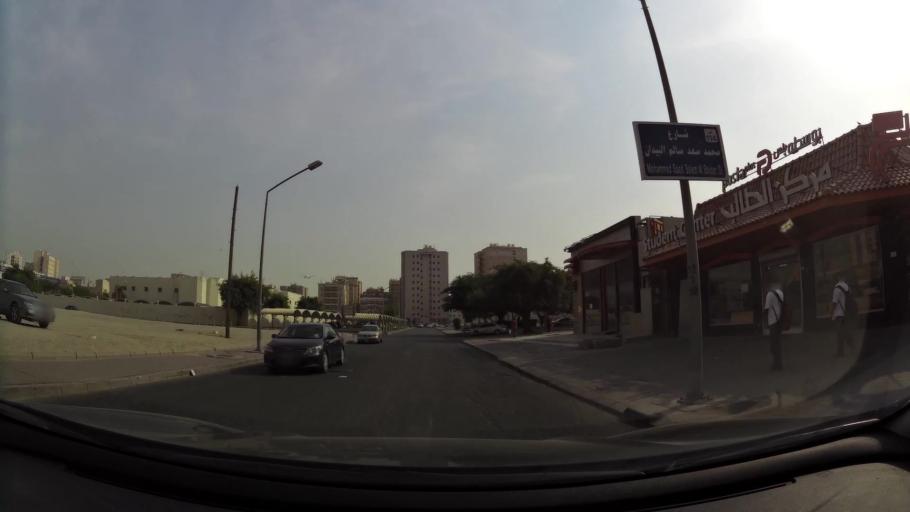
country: KW
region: Al Farwaniyah
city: Al Farwaniyah
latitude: 29.2741
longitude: 47.9608
